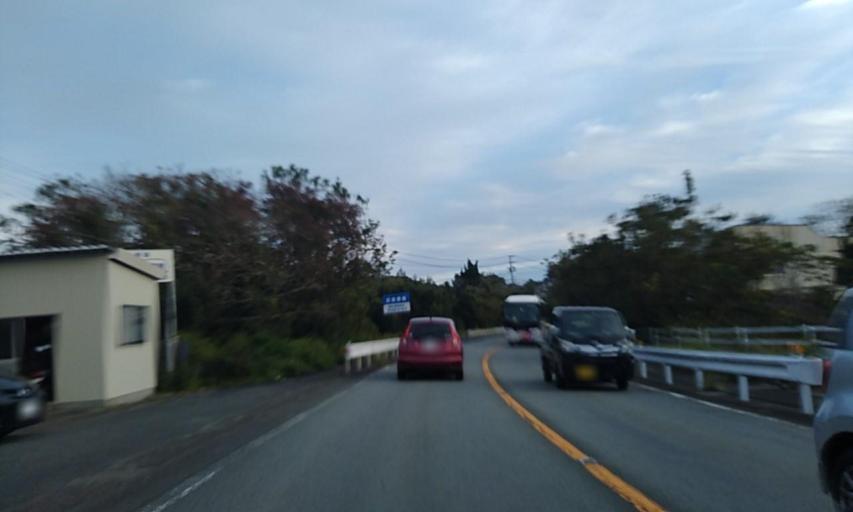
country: JP
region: Mie
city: Toba
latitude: 34.3037
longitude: 136.8756
